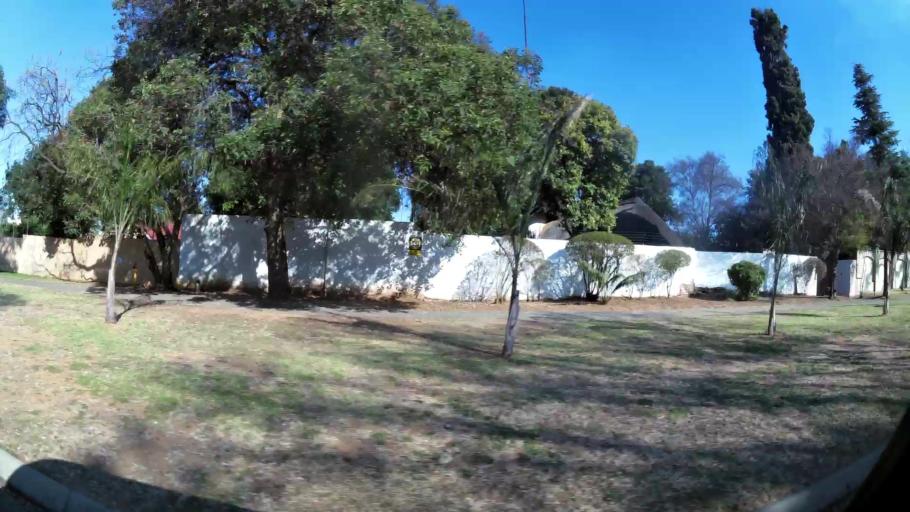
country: ZA
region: Gauteng
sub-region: City of Johannesburg Metropolitan Municipality
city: Roodepoort
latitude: -26.1098
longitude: 27.9548
